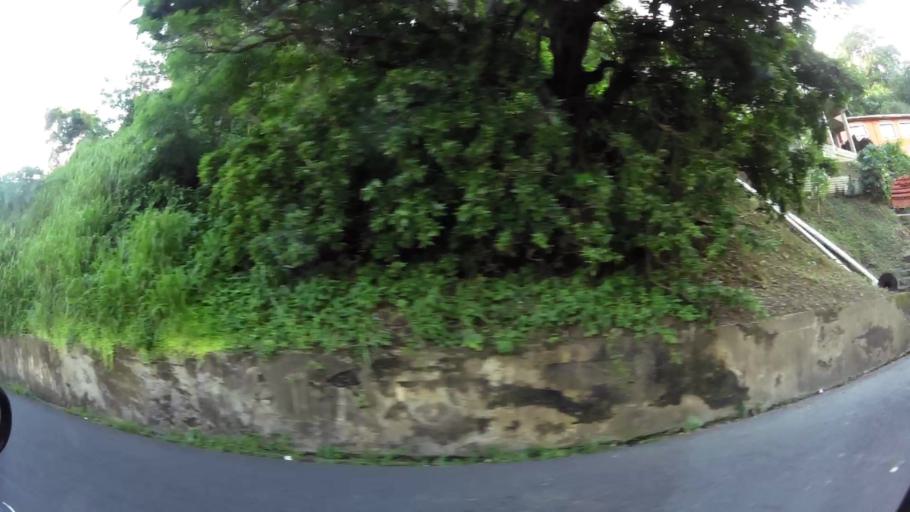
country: TT
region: Eastern Tobago
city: Roxborough
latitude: 11.2192
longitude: -60.6160
